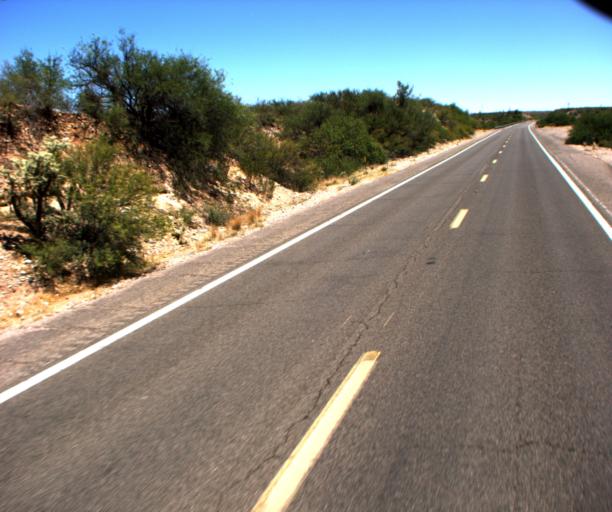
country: US
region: Arizona
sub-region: Pinal County
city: Mammoth
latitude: 32.8177
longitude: -110.6912
